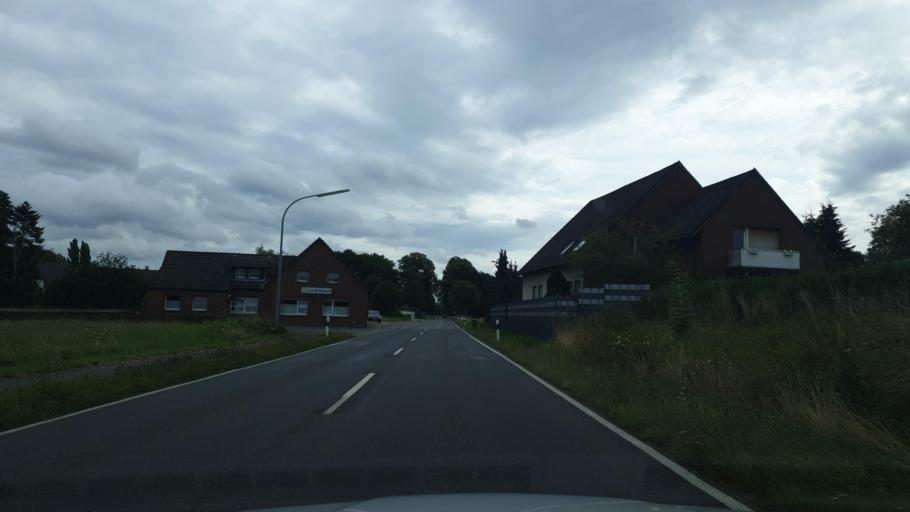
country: DE
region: Lower Saxony
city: Hagen
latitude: 52.2305
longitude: 7.9932
